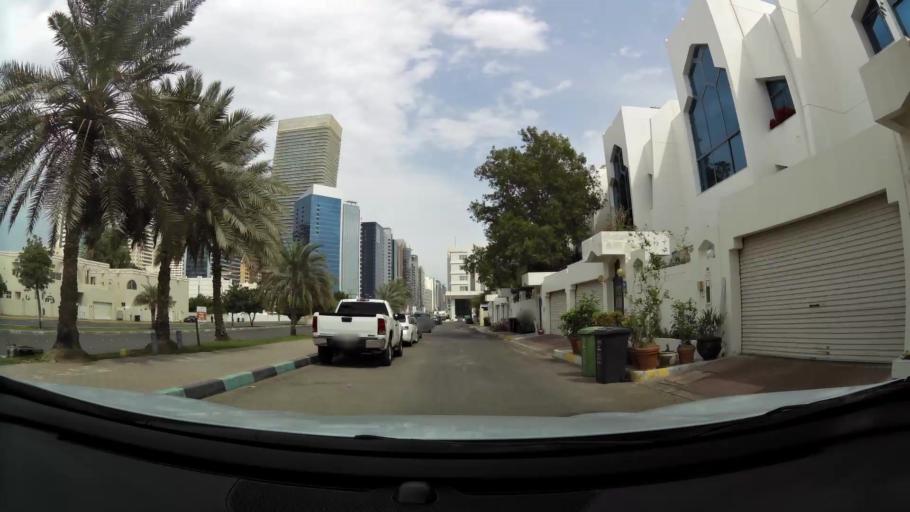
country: AE
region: Abu Dhabi
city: Abu Dhabi
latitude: 24.4650
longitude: 54.3380
